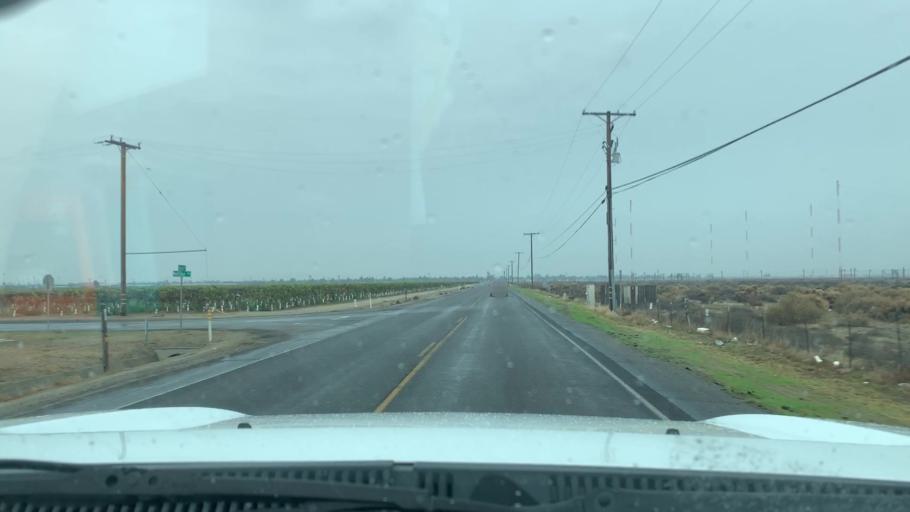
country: US
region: California
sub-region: Kern County
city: Delano
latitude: 35.7613
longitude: -119.2856
